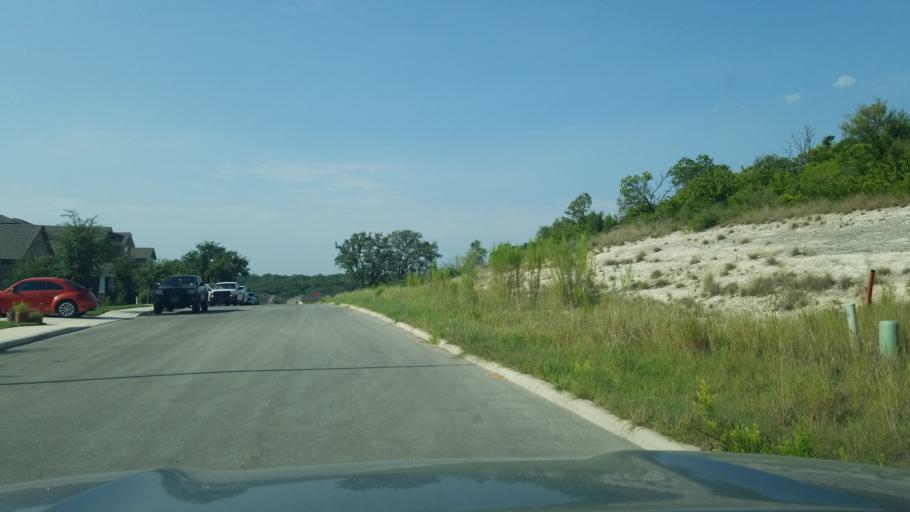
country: US
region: Texas
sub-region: Medina County
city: La Coste
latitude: 29.4041
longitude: -98.7809
